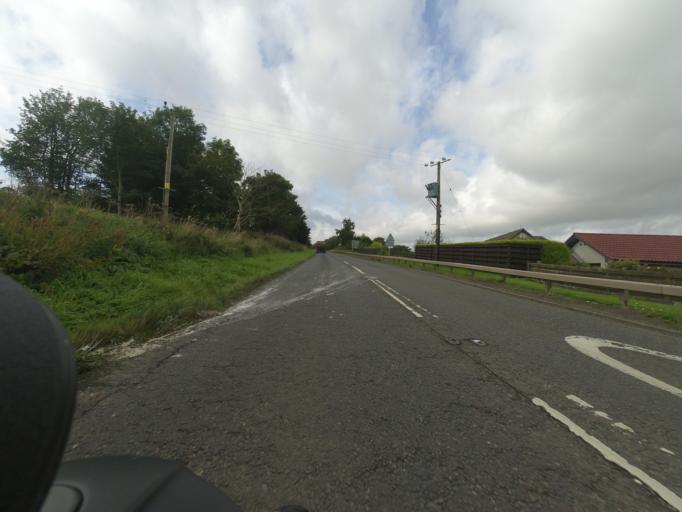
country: GB
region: Scotland
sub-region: Angus
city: Montrose
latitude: 56.6972
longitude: -2.4970
